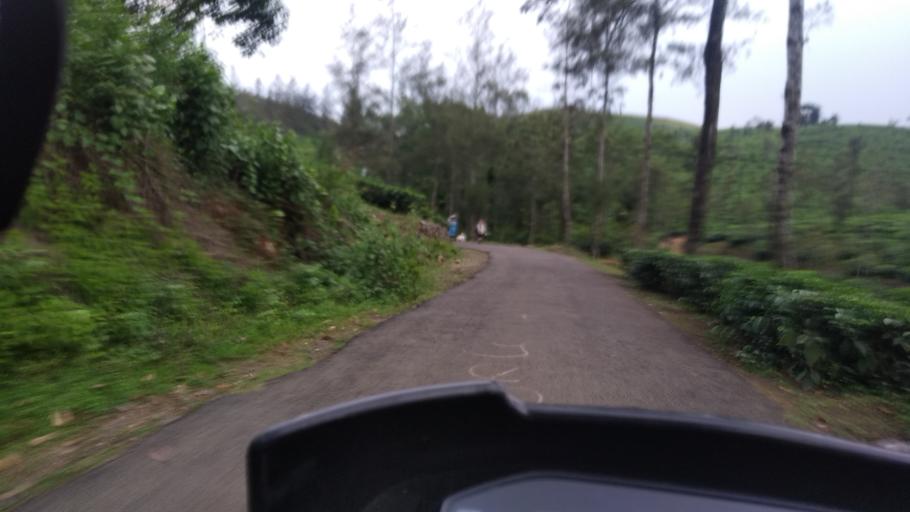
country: IN
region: Tamil Nadu
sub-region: Theni
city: Gudalur
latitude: 9.5443
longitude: 77.0492
